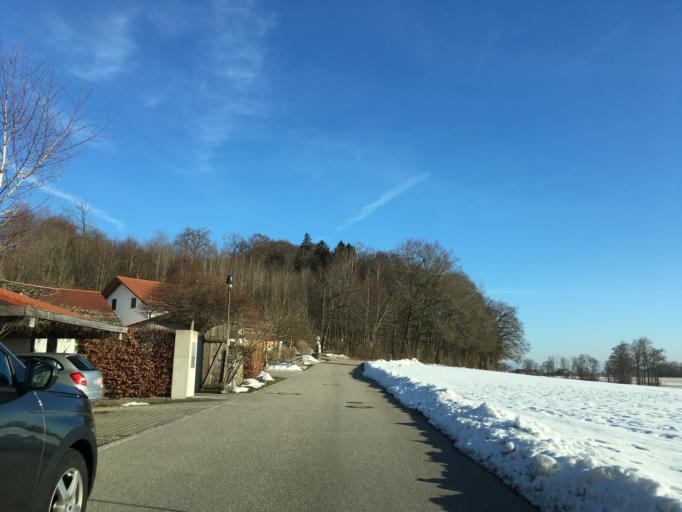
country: DE
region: Bavaria
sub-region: Upper Bavaria
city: Steinhoring
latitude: 48.0990
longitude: 12.0362
